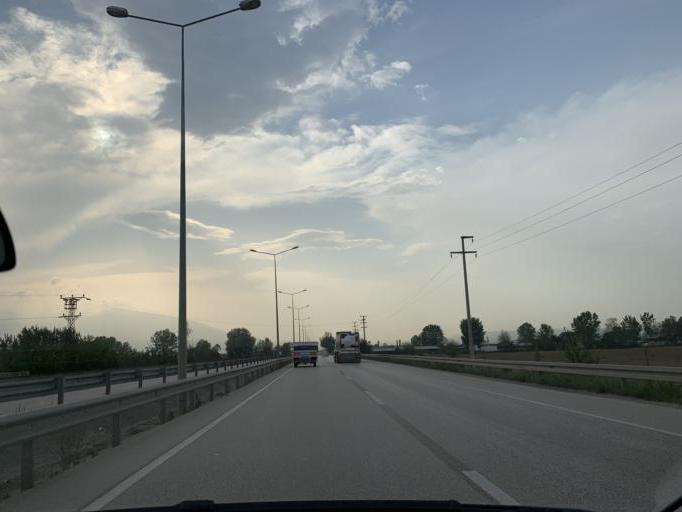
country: TR
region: Bursa
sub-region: Inegoel
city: Inegol
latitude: 40.0688
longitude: 29.5541
